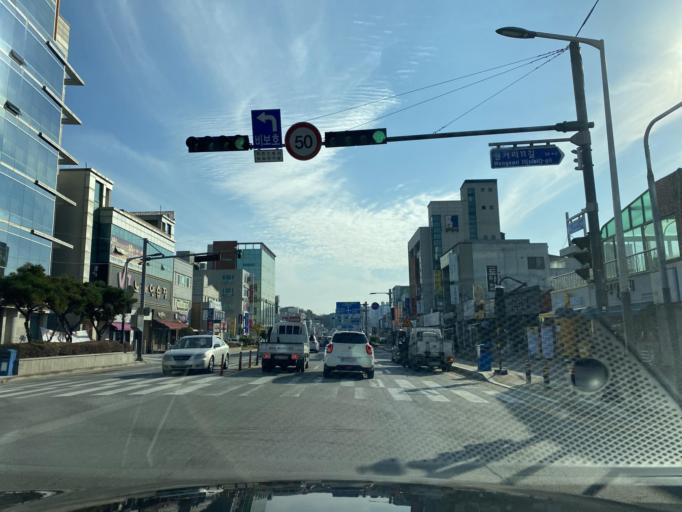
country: KR
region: Chungcheongnam-do
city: Cheonan
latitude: 36.8012
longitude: 127.1590
